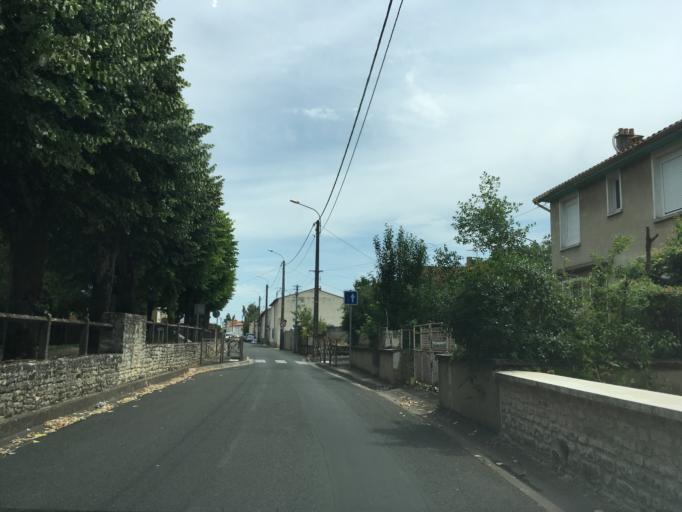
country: FR
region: Poitou-Charentes
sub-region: Departement des Deux-Sevres
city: Niort
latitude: 46.3258
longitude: -0.4841
